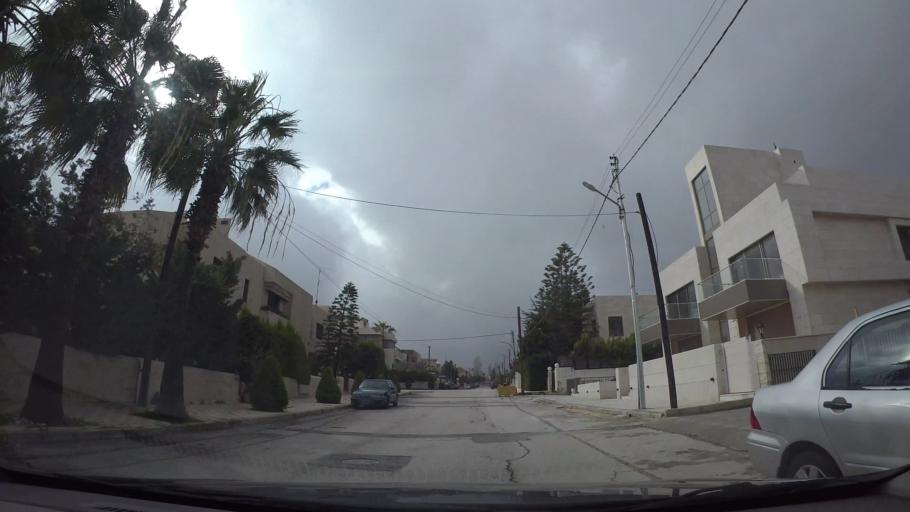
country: JO
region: Amman
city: Amman
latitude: 31.9472
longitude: 35.8945
